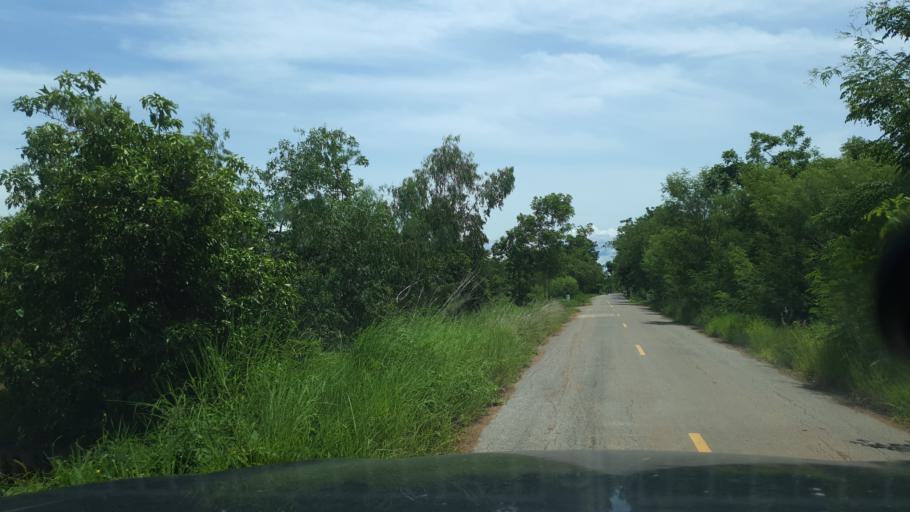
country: TH
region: Sukhothai
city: Ban Na
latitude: 17.1057
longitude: 99.6785
